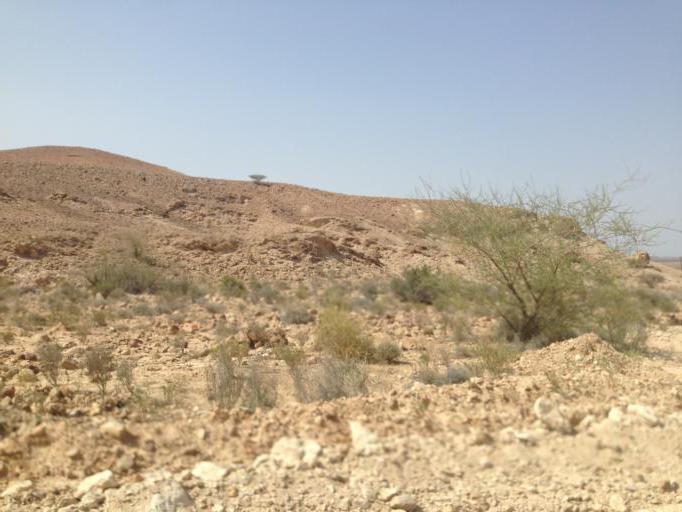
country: OM
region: Ash Sharqiyah
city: Ibra'
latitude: 23.0799
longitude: 58.9040
